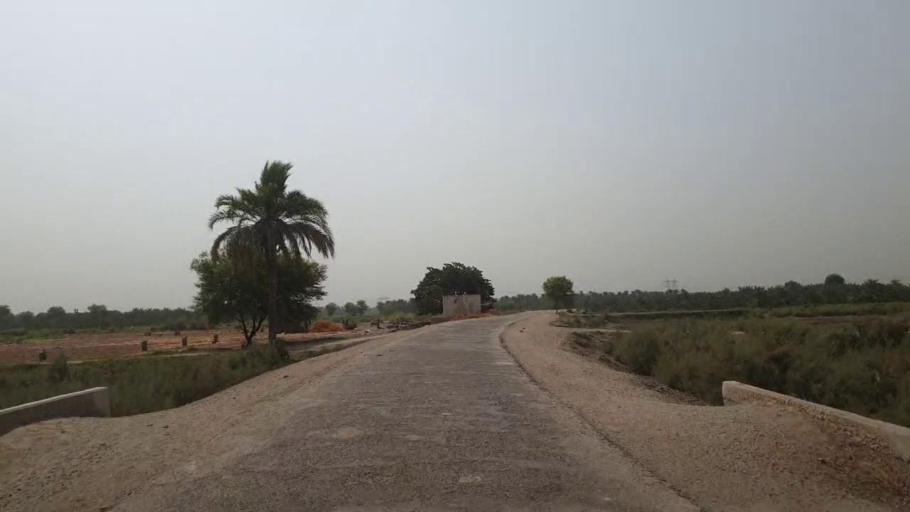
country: PK
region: Sindh
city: Gambat
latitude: 27.4204
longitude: 68.5468
